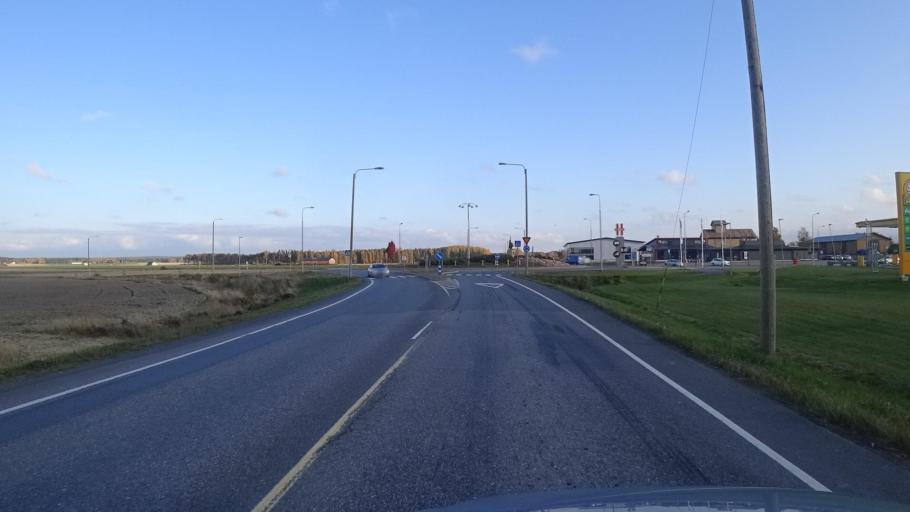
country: FI
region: Satakunta
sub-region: Rauma
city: Saekylae
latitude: 61.0470
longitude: 22.3577
